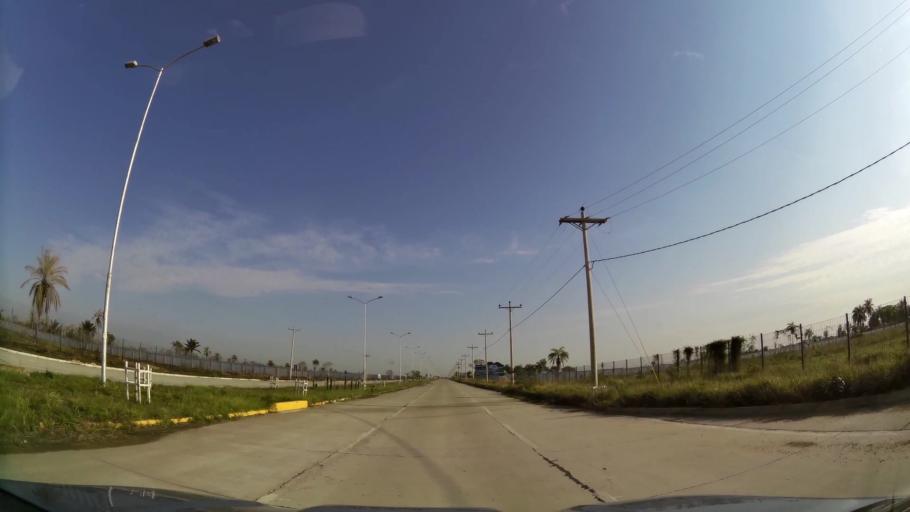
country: BO
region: Santa Cruz
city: Santa Cruz de la Sierra
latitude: -17.6856
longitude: -63.1175
